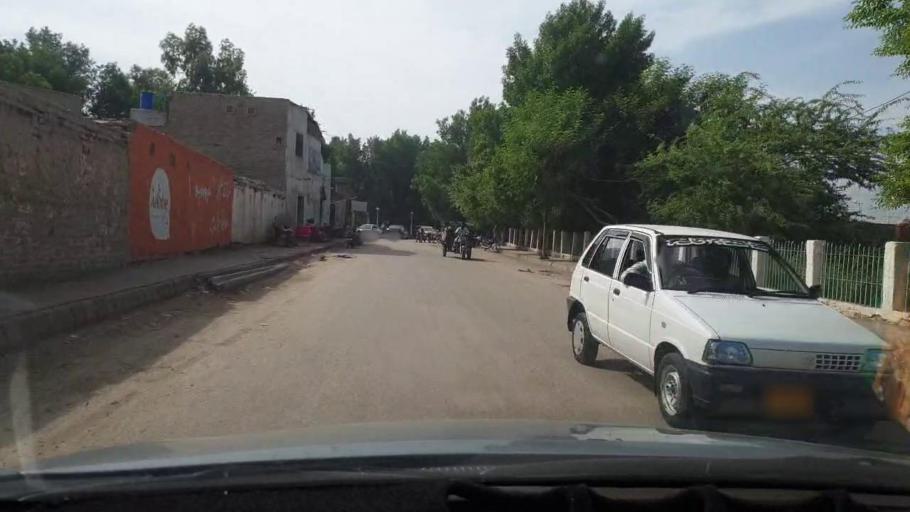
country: PK
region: Sindh
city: Khairpur
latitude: 27.5367
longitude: 68.7525
